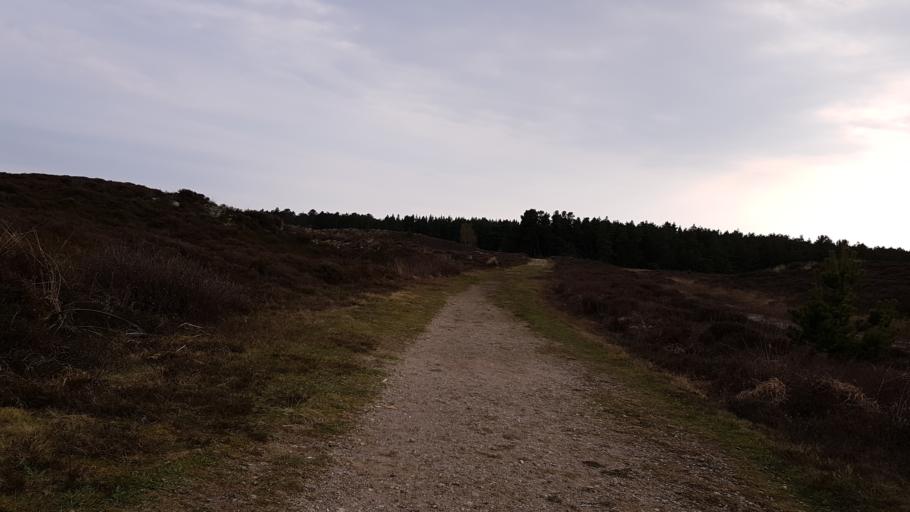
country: DE
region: Schleswig-Holstein
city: List
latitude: 55.1556
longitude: 8.5328
